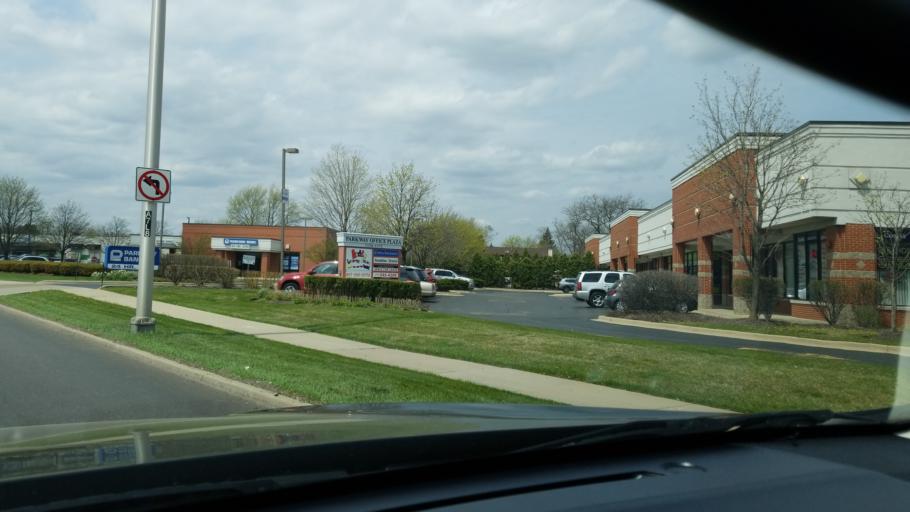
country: US
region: Illinois
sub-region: Cook County
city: Rolling Meadows
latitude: 42.0558
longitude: -88.0001
